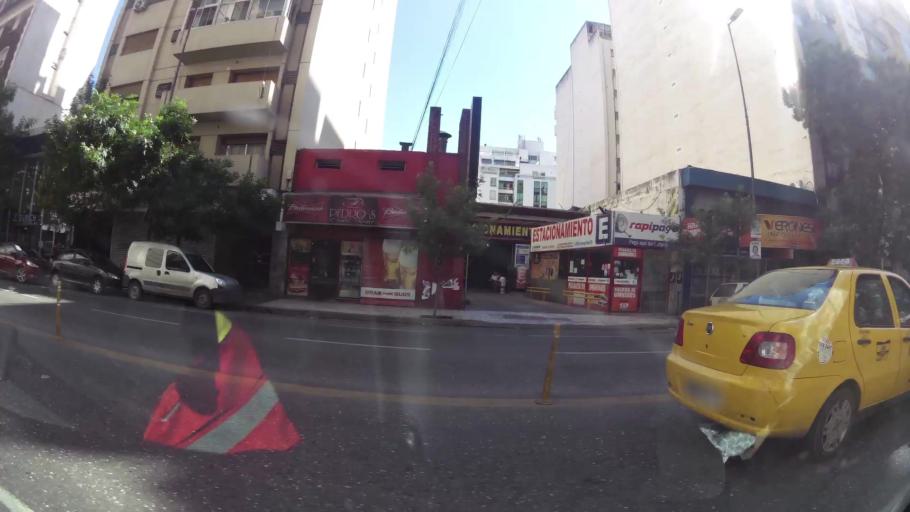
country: AR
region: Cordoba
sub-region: Departamento de Capital
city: Cordoba
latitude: -31.4109
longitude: -64.1921
